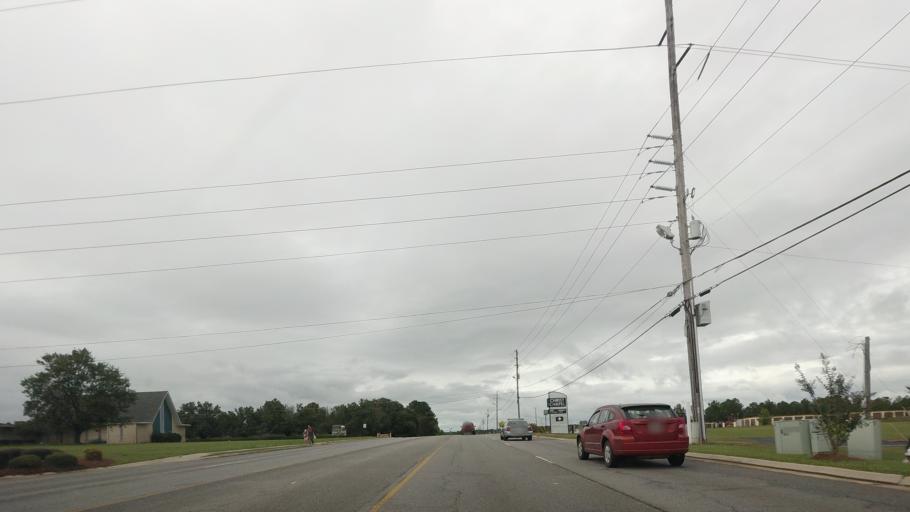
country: US
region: Georgia
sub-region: Houston County
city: Warner Robins
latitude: 32.5890
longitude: -83.6227
